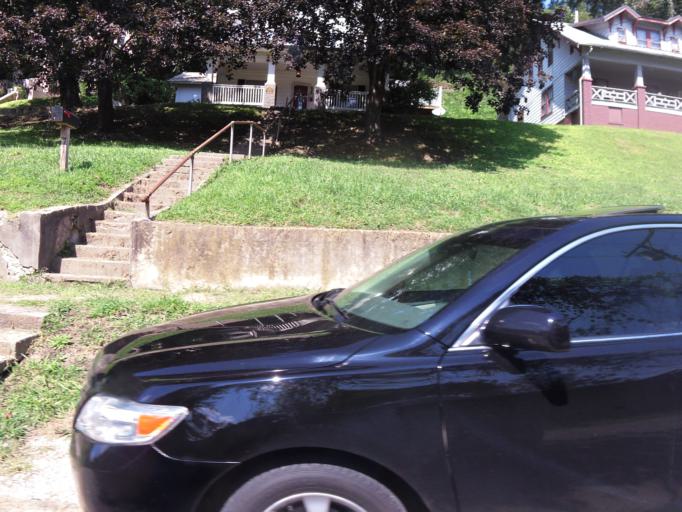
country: US
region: Kentucky
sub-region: Harlan County
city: Harlan
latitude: 36.8484
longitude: -83.3192
